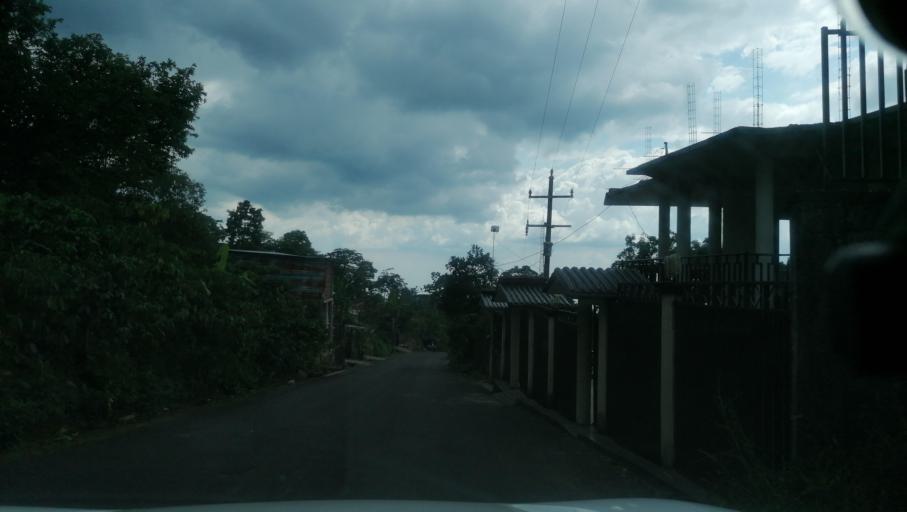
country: MX
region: Chiapas
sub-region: Cacahoatan
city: Benito Juarez
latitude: 15.0817
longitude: -92.1971
